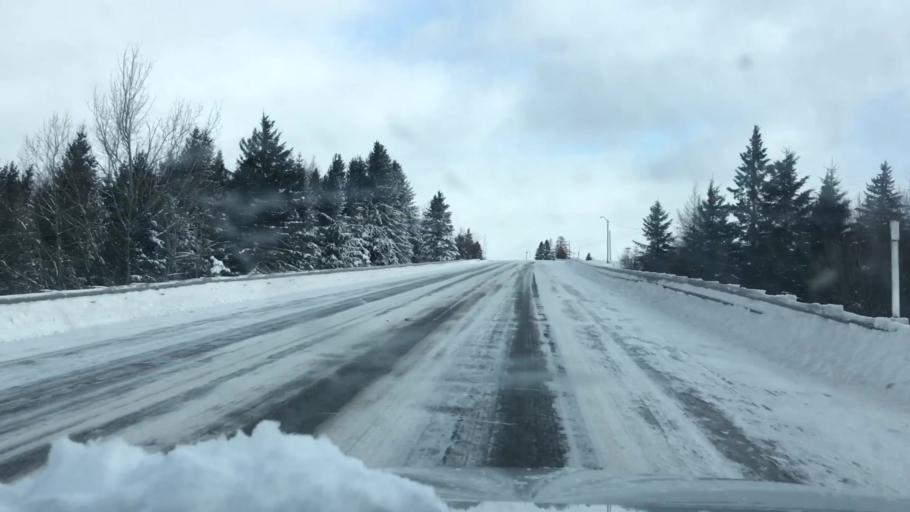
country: US
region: Maine
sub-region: Aroostook County
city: Van Buren
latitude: 47.0957
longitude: -67.9781
